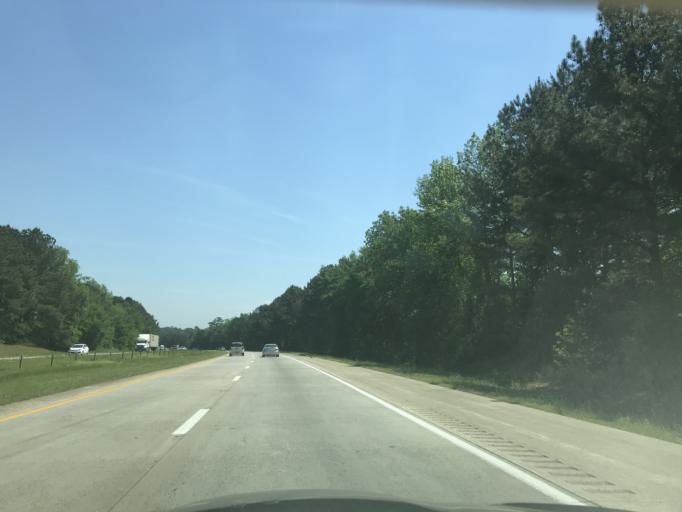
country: US
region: North Carolina
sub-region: Johnston County
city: Benson
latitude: 35.4695
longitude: -78.5484
